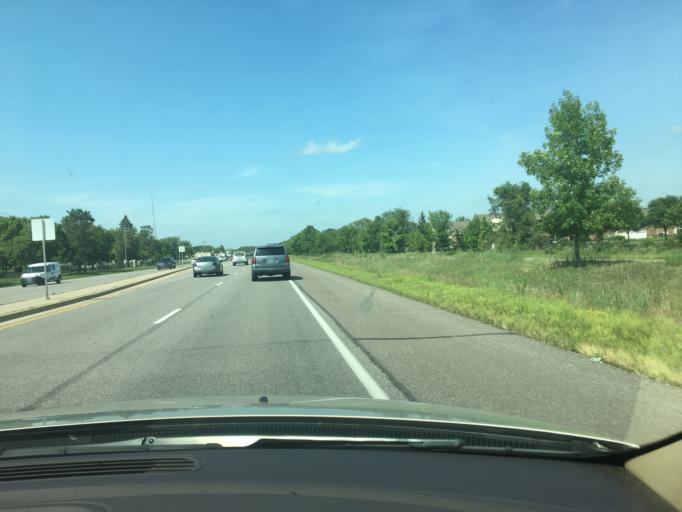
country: US
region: Minnesota
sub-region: Stearns County
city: Saint Cloud
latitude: 45.5293
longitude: -94.1633
